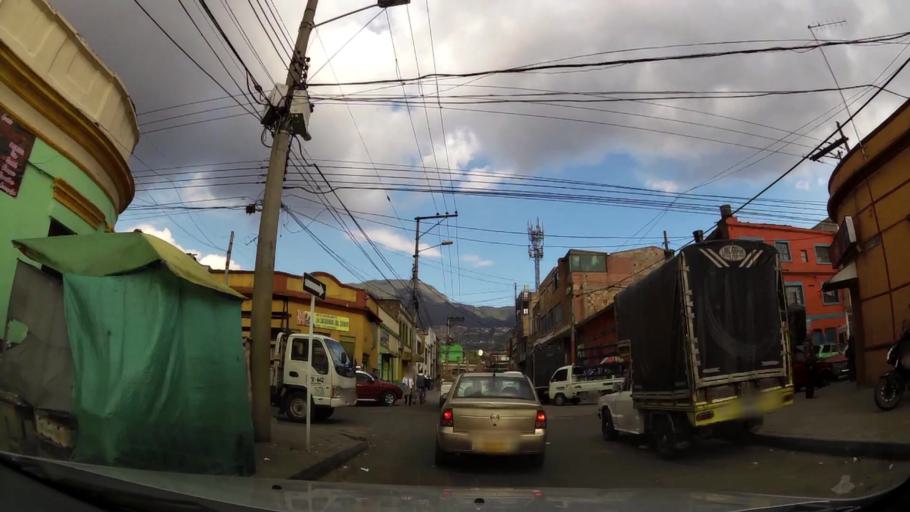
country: CO
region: Bogota D.C.
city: Bogota
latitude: 4.5919
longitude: -74.0845
